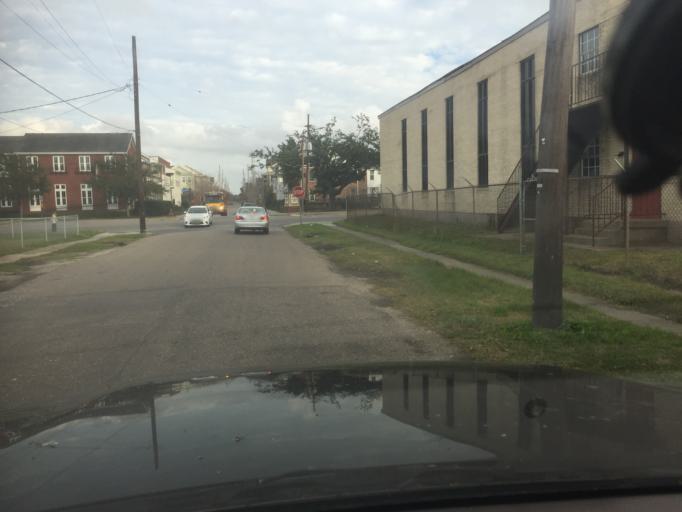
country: US
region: Louisiana
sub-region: Orleans Parish
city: New Orleans
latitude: 29.9947
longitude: -90.0789
